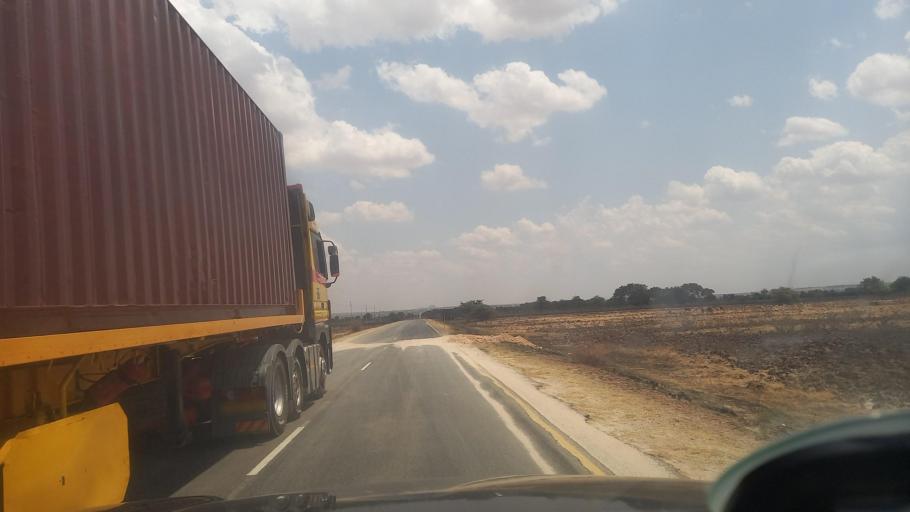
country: TZ
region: Dodoma
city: Kongwa
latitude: -6.0837
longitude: 36.5924
